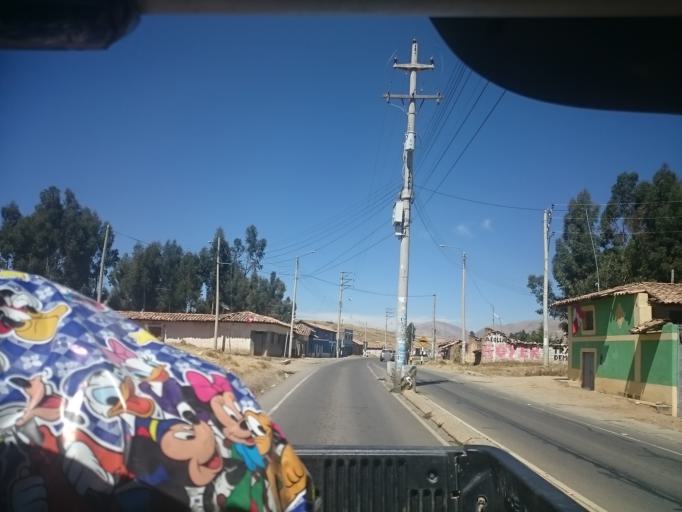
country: PE
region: Junin
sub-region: Provincia de Jauja
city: Acolla
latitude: -11.7456
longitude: -75.5374
